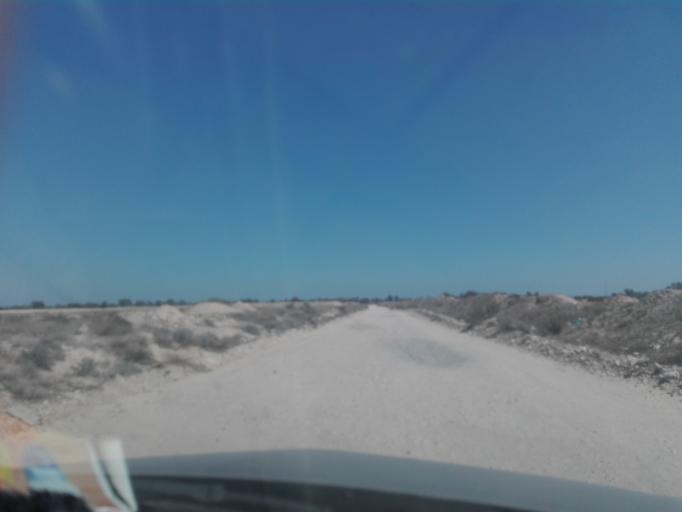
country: TN
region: Qabis
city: Gabes
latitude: 33.8722
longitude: 10.0160
